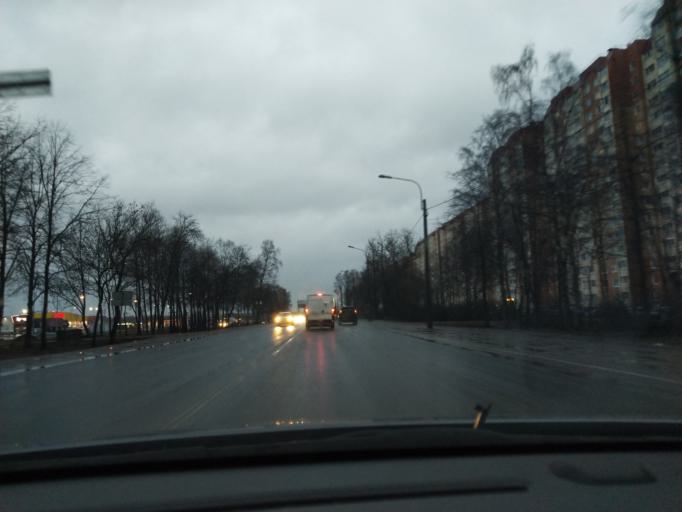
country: RU
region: St.-Petersburg
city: Gorelovo
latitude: 59.7918
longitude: 30.1471
